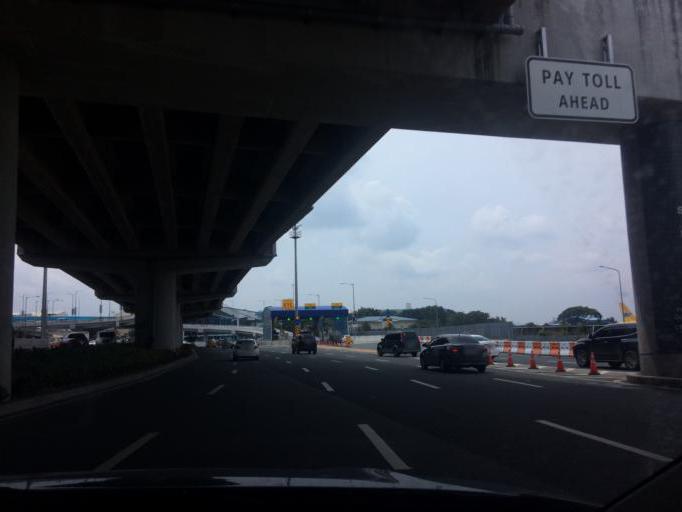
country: PH
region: Metro Manila
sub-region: Makati City
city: Makati City
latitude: 14.5187
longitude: 121.0172
